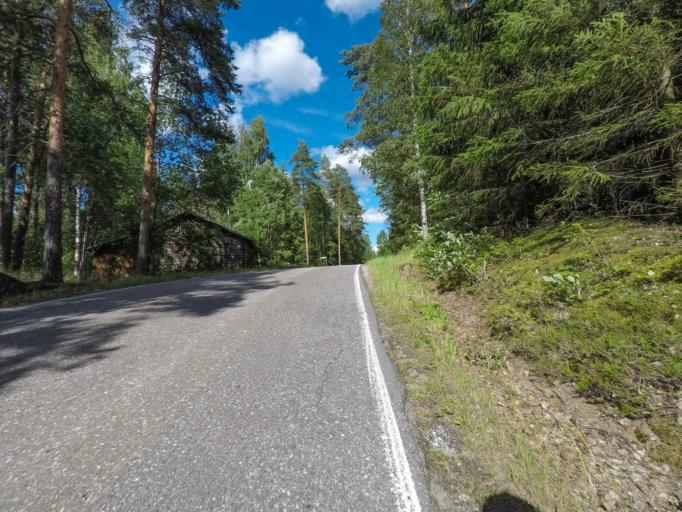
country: FI
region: South Karelia
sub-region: Lappeenranta
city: Joutseno
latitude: 61.1114
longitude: 28.3699
